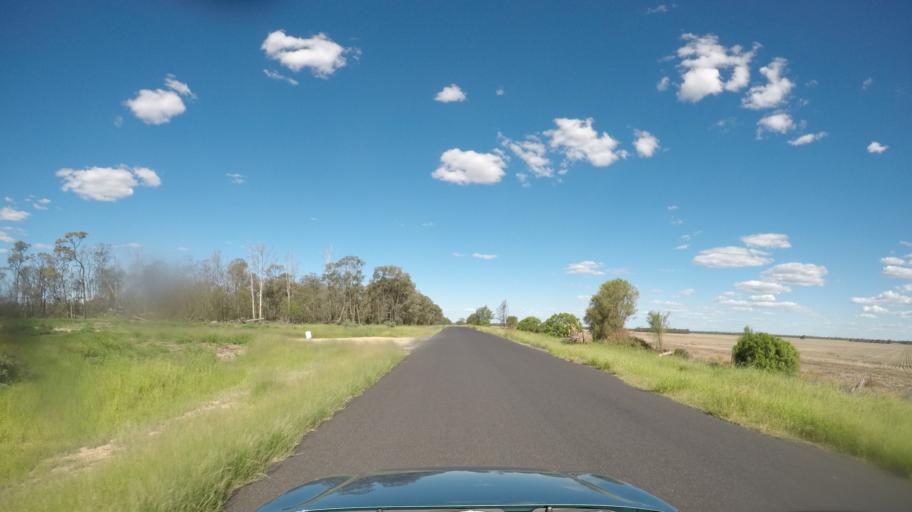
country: AU
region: Queensland
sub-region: Goondiwindi
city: Goondiwindi
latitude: -28.1635
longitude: 150.4248
